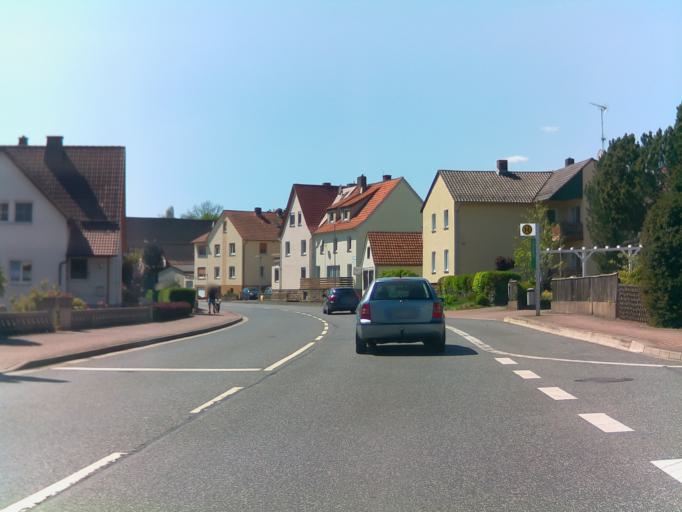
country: DE
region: Hesse
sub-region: Regierungsbezirk Kassel
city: Niederaula
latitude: 50.7749
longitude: 9.5724
